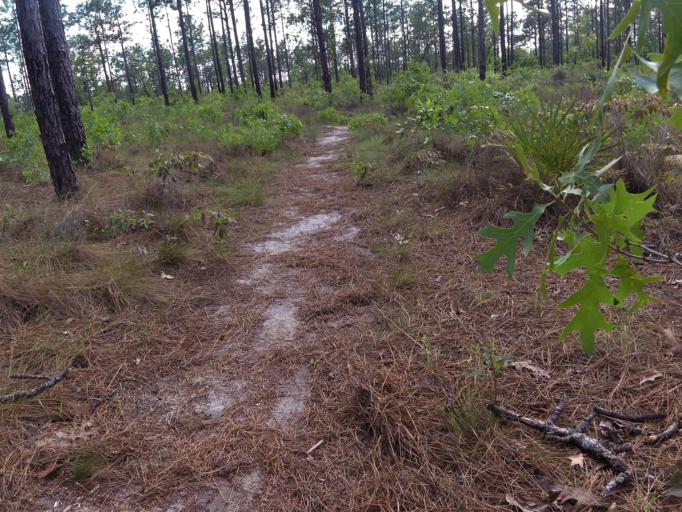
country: US
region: Florida
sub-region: Clay County
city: Keystone Heights
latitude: 29.8396
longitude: -81.9481
